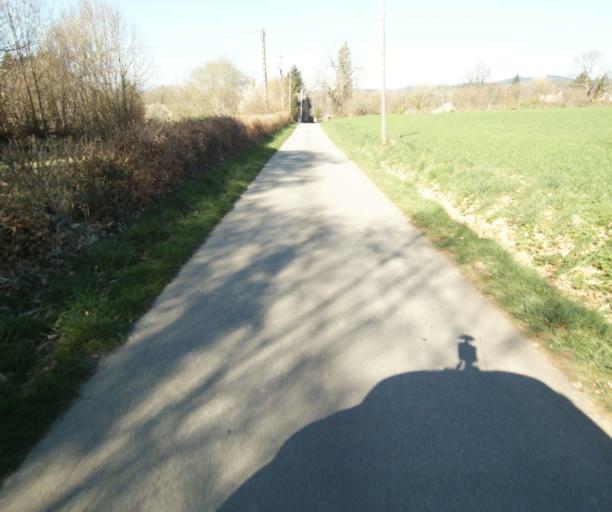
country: FR
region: Limousin
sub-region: Departement de la Correze
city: Chamboulive
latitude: 45.4803
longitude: 1.7400
